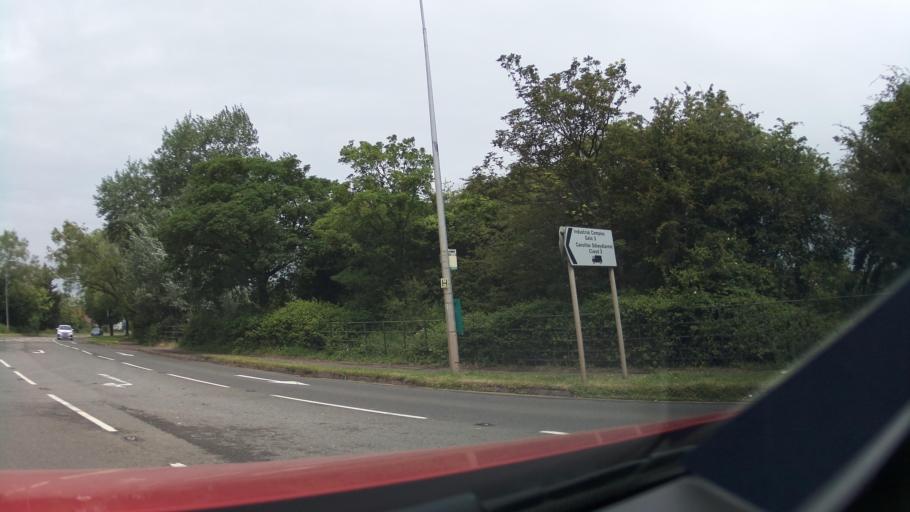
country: GB
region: Wales
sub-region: Vale of Glamorgan
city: Dinas Powys
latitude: 51.4082
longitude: -3.2271
